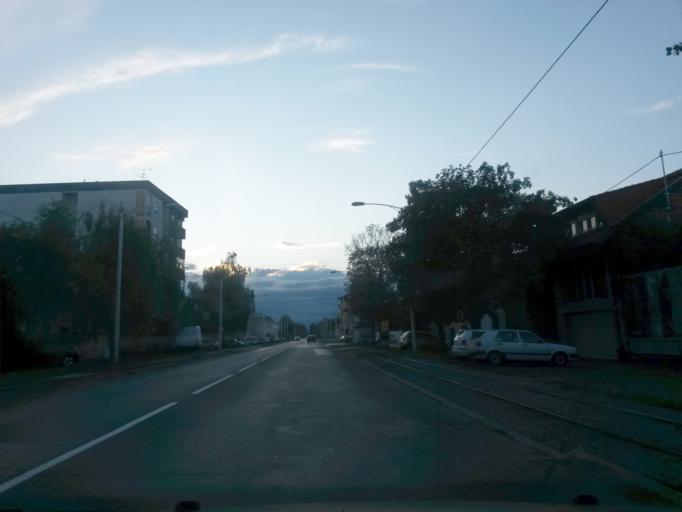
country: HR
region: Osjecko-Baranjska
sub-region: Grad Osijek
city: Osijek
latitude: 45.5530
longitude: 18.7282
